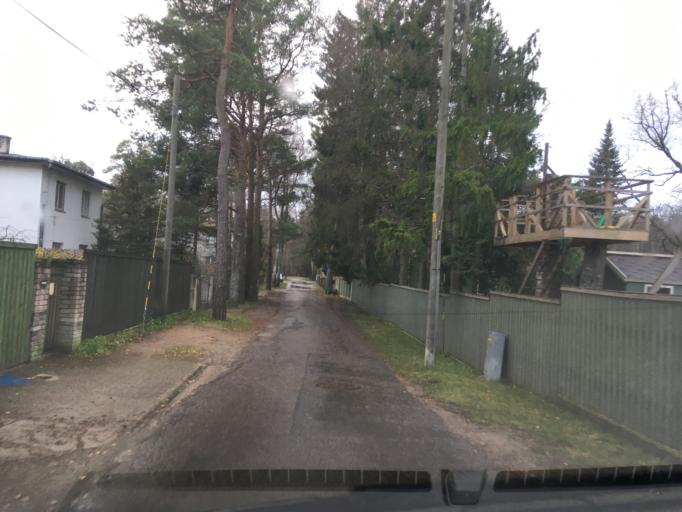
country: EE
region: Harju
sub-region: Tallinna linn
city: Tallinn
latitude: 59.3741
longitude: 24.7113
